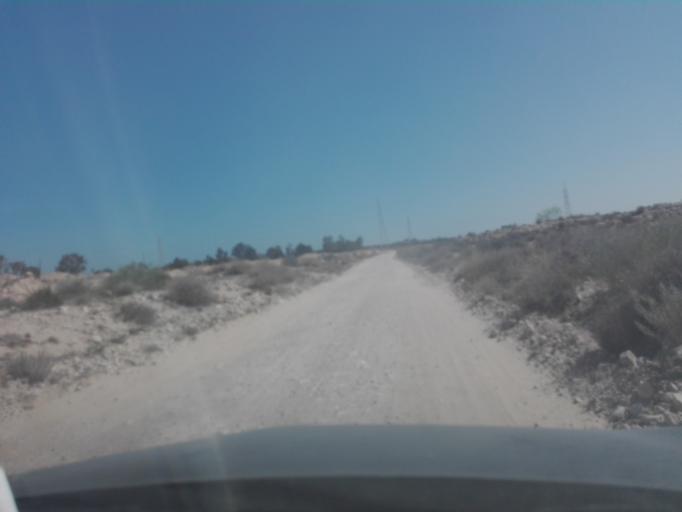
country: TN
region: Qabis
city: Gabes
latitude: 33.8751
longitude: 10.0264
